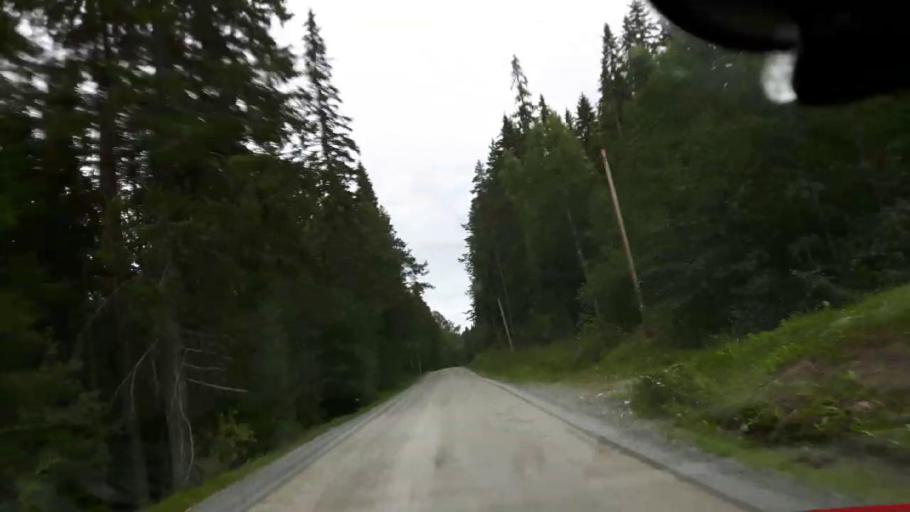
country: SE
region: Jaemtland
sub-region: Braecke Kommun
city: Braecke
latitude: 63.0891
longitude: 15.2590
